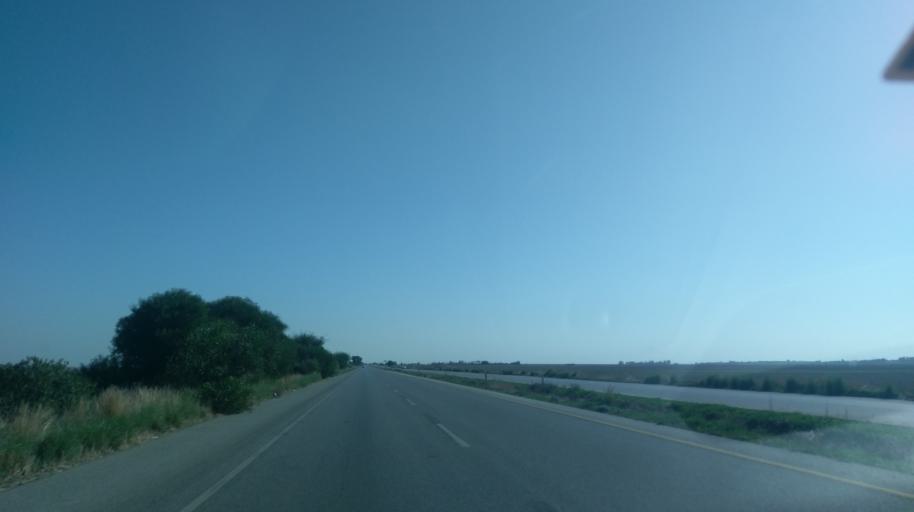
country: CY
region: Ammochostos
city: Lefkonoiko
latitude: 35.1851
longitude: 33.6690
